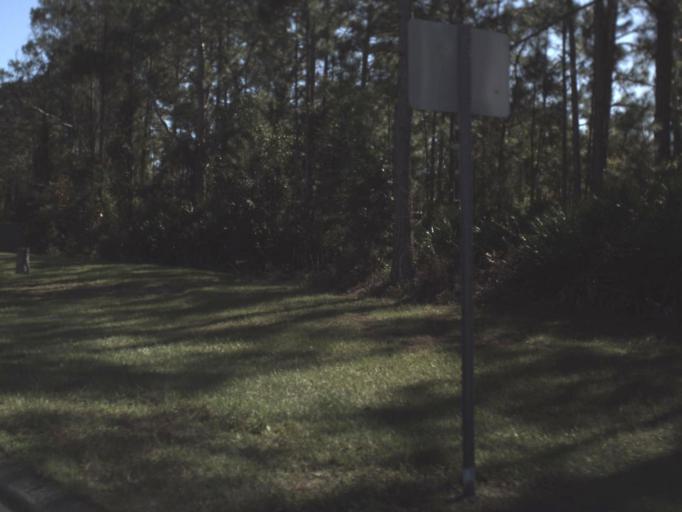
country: US
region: Florida
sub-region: Flagler County
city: Palm Coast
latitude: 29.5515
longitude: -81.2469
